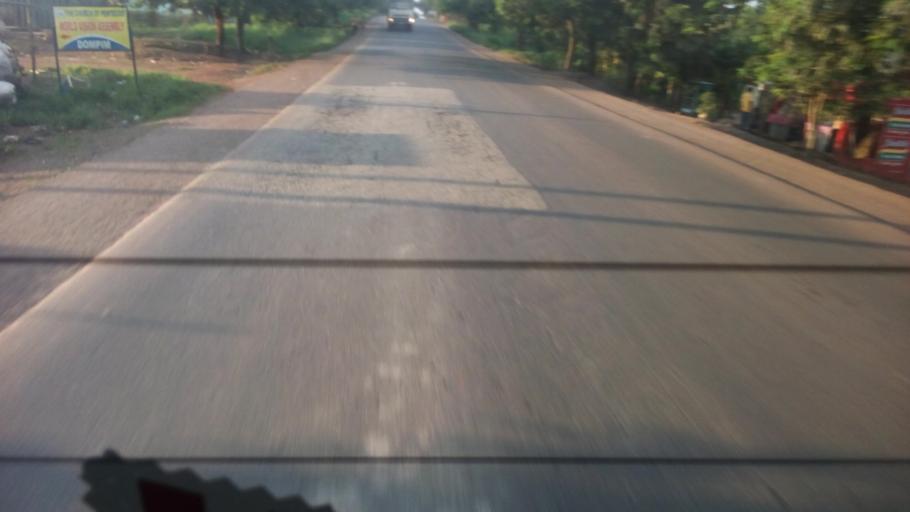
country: GH
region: Western
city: Tarkwa
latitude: 5.1571
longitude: -2.0754
